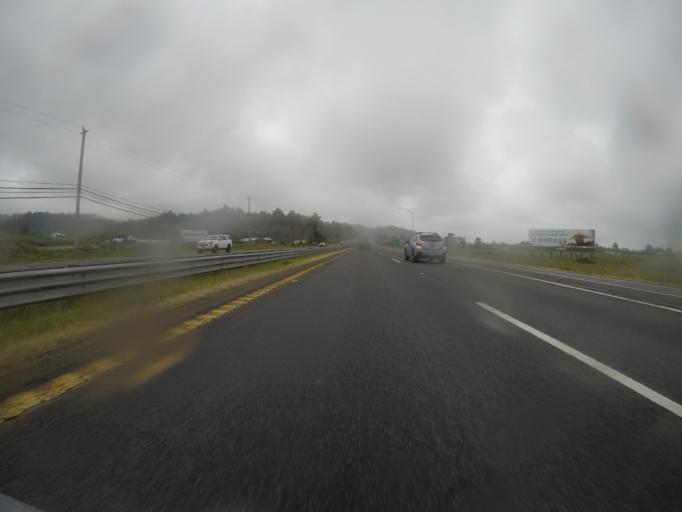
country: US
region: California
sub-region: Humboldt County
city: Arcata
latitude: 40.8953
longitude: -124.0824
